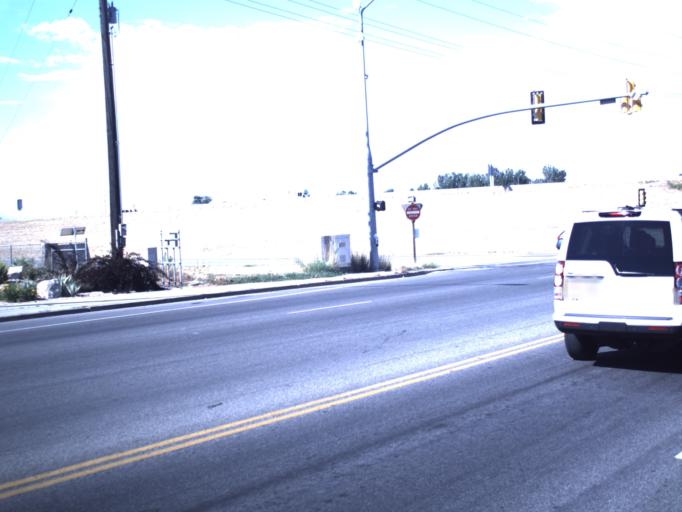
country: US
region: Utah
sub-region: Davis County
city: Kaysville
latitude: 41.0382
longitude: -111.9467
